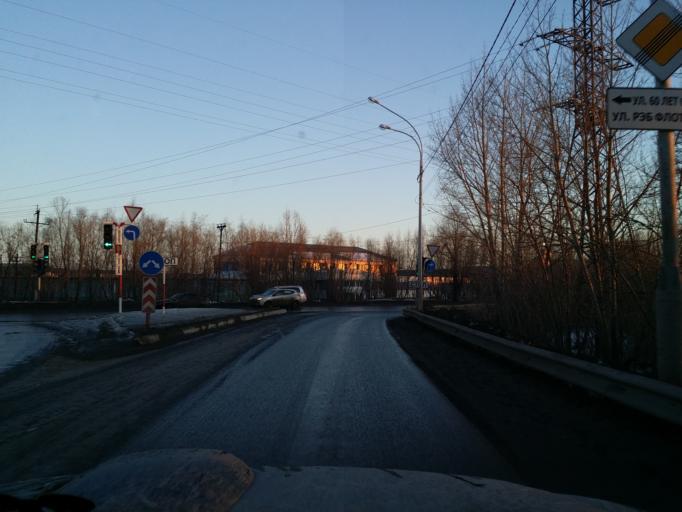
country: RU
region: Khanty-Mansiyskiy Avtonomnyy Okrug
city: Nizhnevartovsk
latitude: 60.9274
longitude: 76.5315
